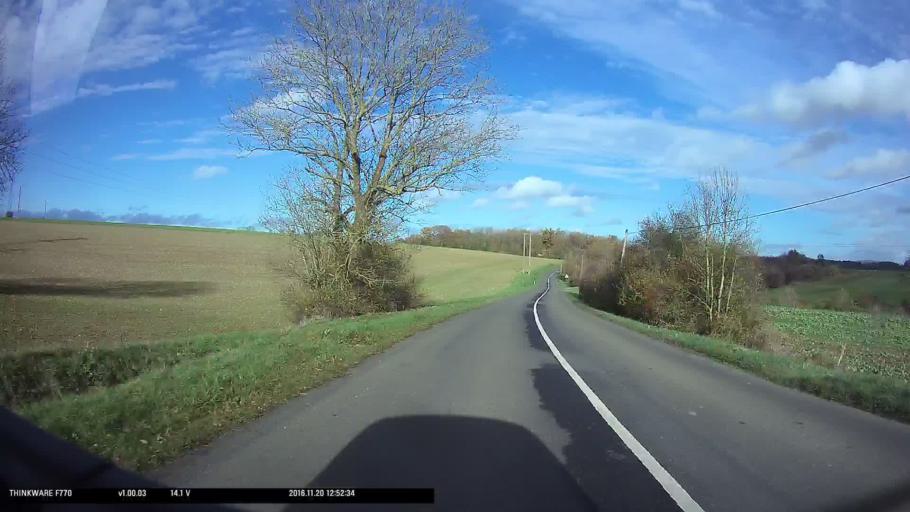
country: FR
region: Ile-de-France
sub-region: Departement du Val-d'Oise
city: Ableiges
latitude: 49.0832
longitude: 1.9776
